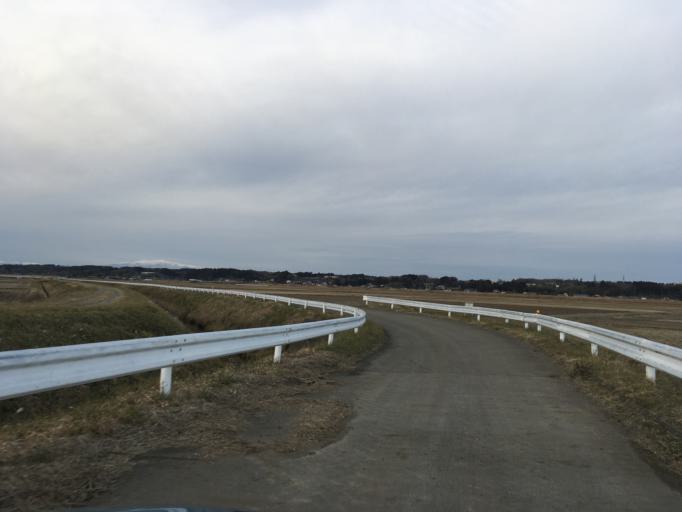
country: JP
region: Miyagi
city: Kogota
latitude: 38.6393
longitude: 141.0671
